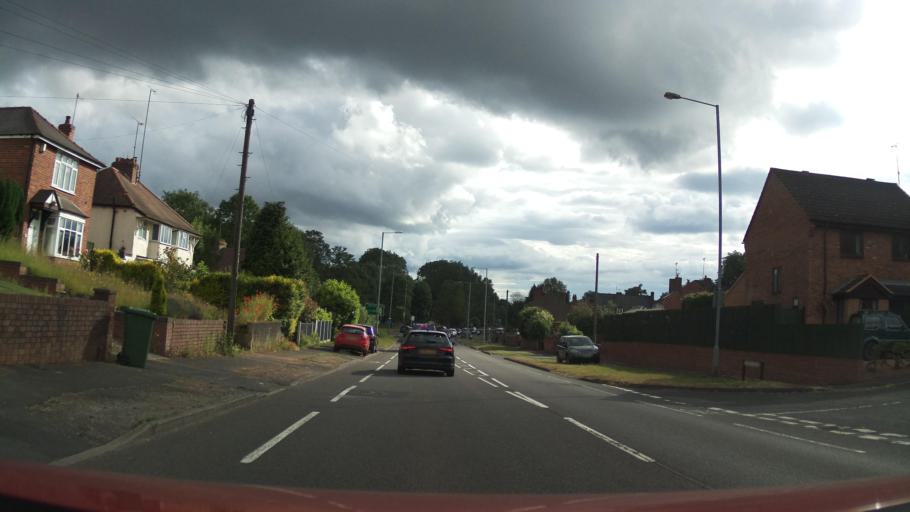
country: GB
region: England
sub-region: Worcestershire
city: Kidderminster
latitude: 52.4015
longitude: -2.2318
